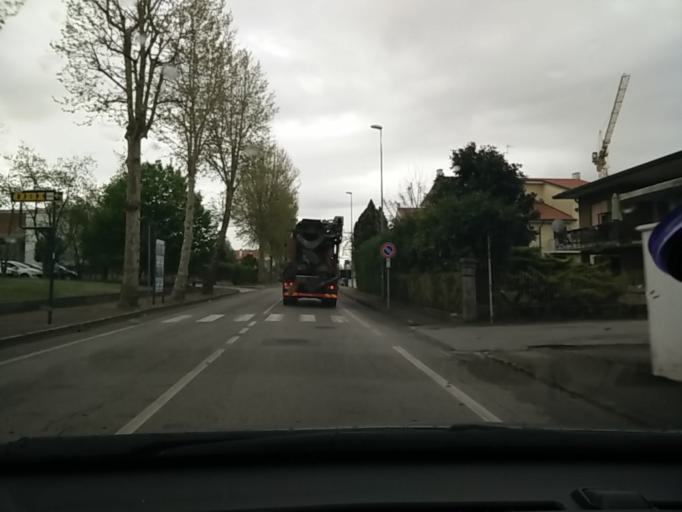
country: IT
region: Veneto
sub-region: Provincia di Treviso
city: Silea
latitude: 45.6530
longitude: 12.3026
